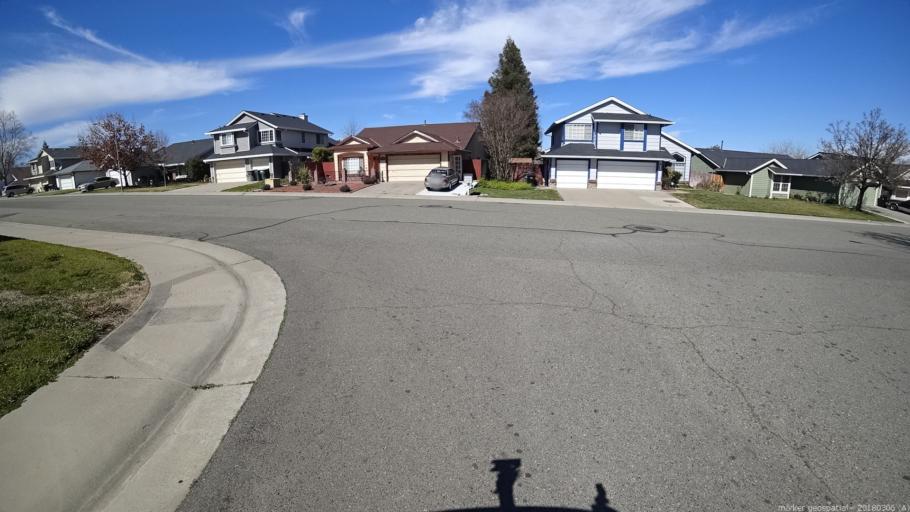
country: US
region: California
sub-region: Sacramento County
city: Vineyard
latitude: 38.4670
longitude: -121.3580
